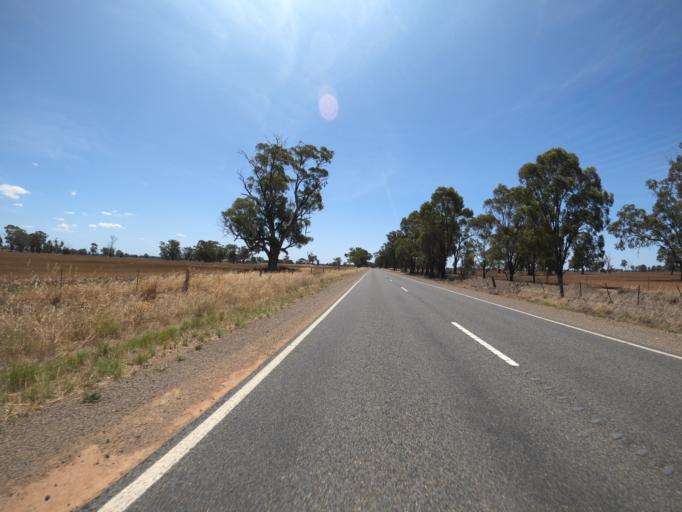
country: AU
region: Victoria
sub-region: Moira
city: Yarrawonga
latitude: -36.2053
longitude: 145.9672
